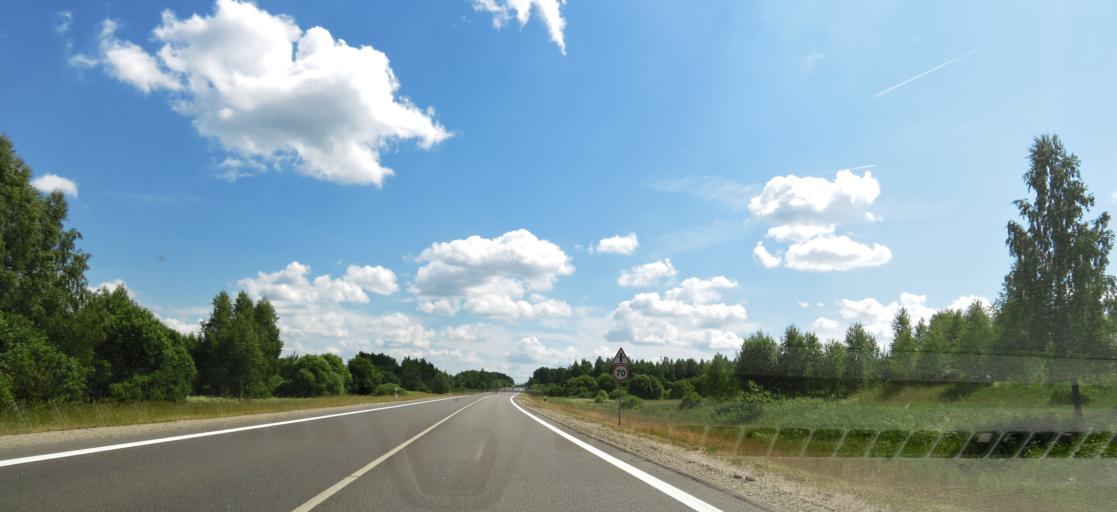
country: LT
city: Skaidiskes
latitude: 54.5589
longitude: 25.6621
